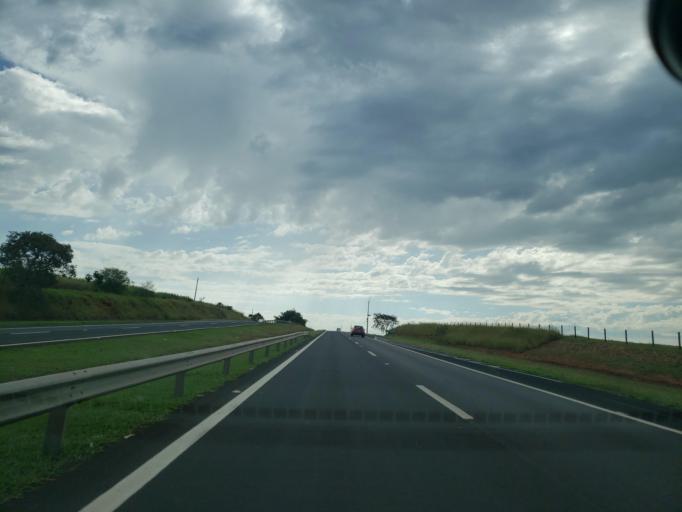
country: BR
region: Sao Paulo
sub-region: Cafelandia
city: Cafelandia
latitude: -21.7766
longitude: -49.6618
